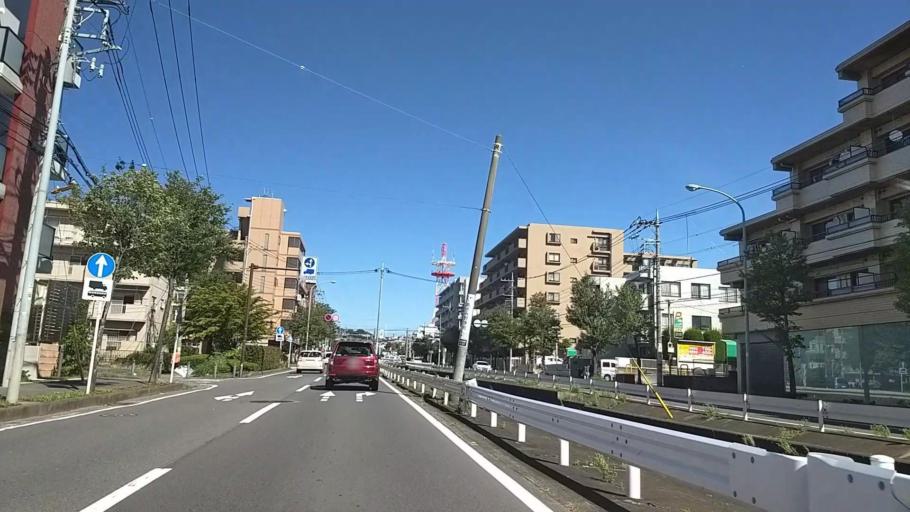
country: JP
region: Tokyo
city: Chofugaoka
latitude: 35.5755
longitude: 139.5490
